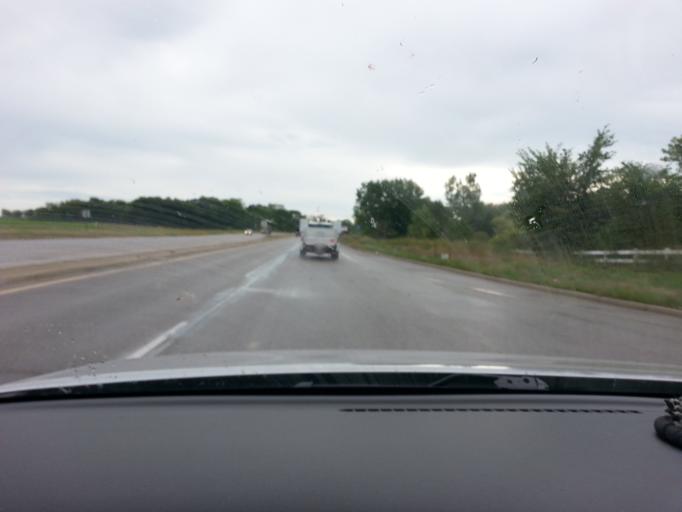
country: US
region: Minnesota
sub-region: Scott County
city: Prior Lake
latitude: 44.6948
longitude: -93.3788
